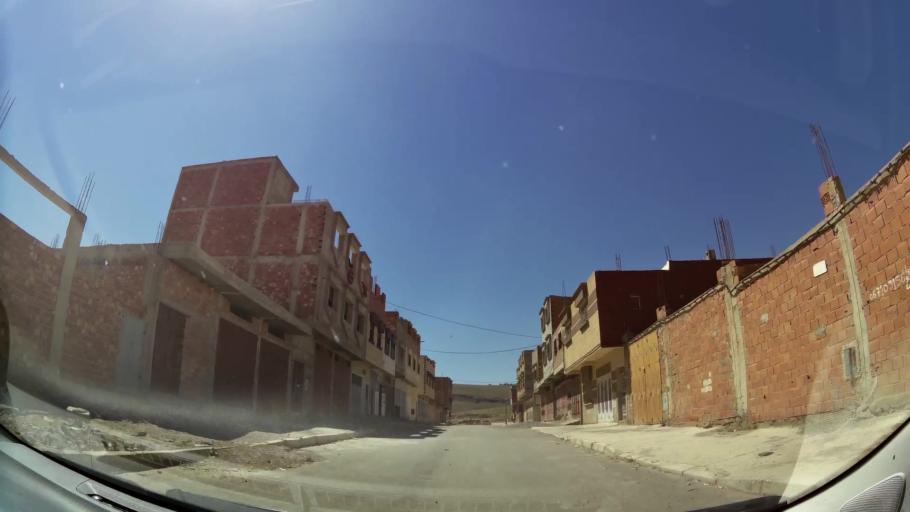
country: MA
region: Oriental
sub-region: Oujda-Angad
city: Oujda
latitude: 34.6491
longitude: -1.8727
